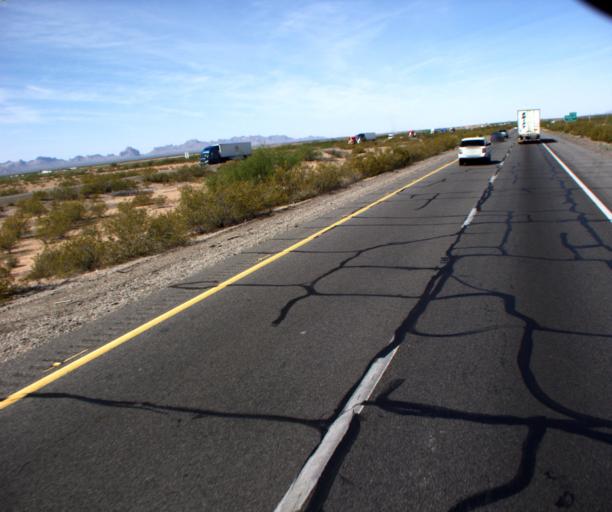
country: US
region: Arizona
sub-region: La Paz County
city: Salome
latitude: 33.5344
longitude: -113.1396
